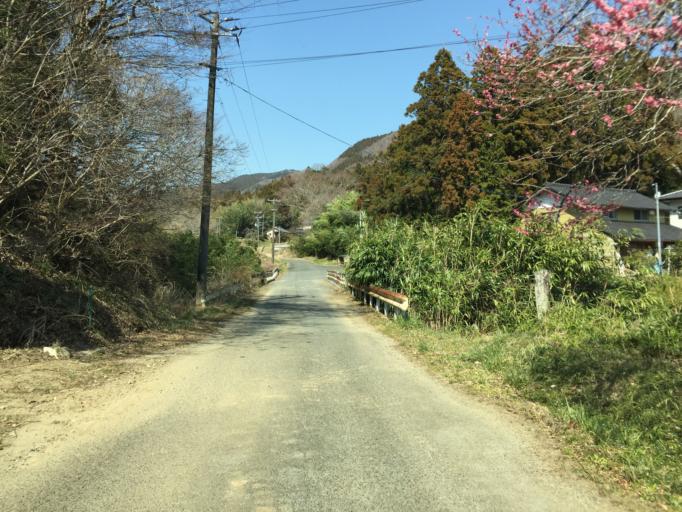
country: JP
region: Fukushima
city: Iwaki
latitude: 37.0107
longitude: 140.7902
